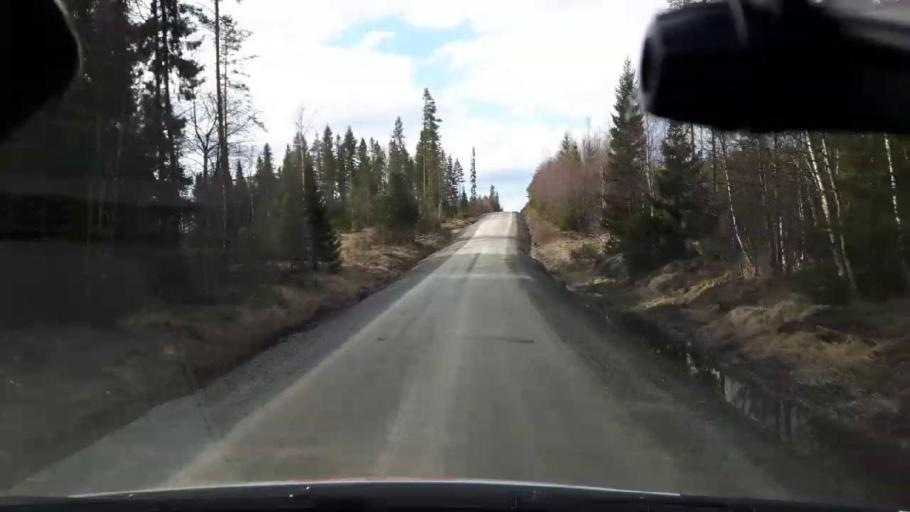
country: SE
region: Jaemtland
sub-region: Bergs Kommun
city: Hoverberg
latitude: 62.8947
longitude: 14.6522
